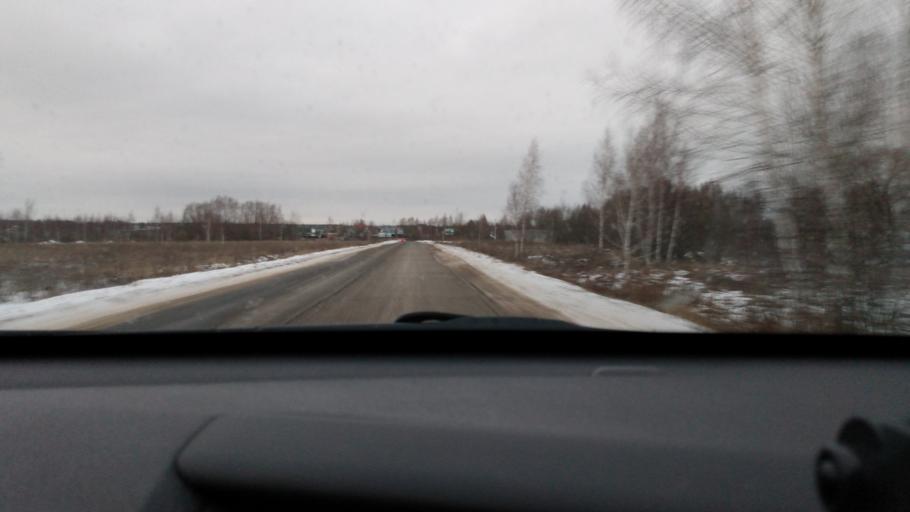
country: RU
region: Moskovskaya
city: Meshcherino
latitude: 55.3101
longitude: 38.3321
